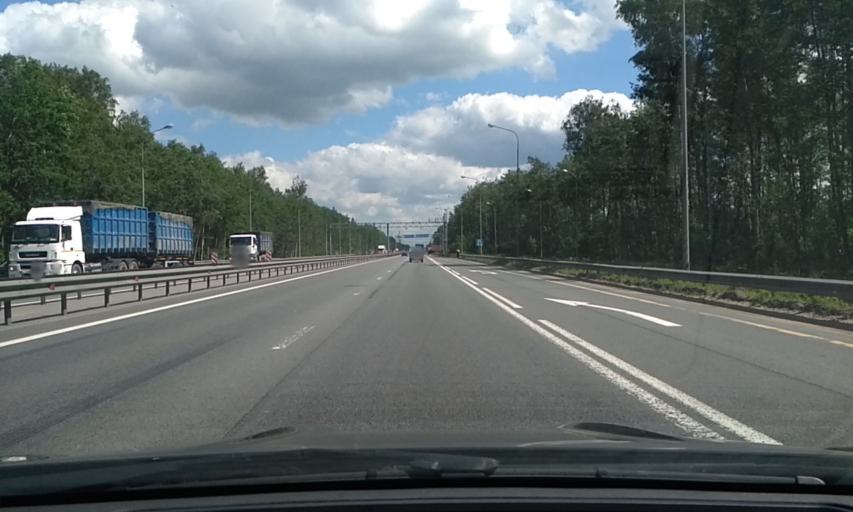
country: RU
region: Leningrad
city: Rybatskoye
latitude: 59.8927
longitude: 30.5369
